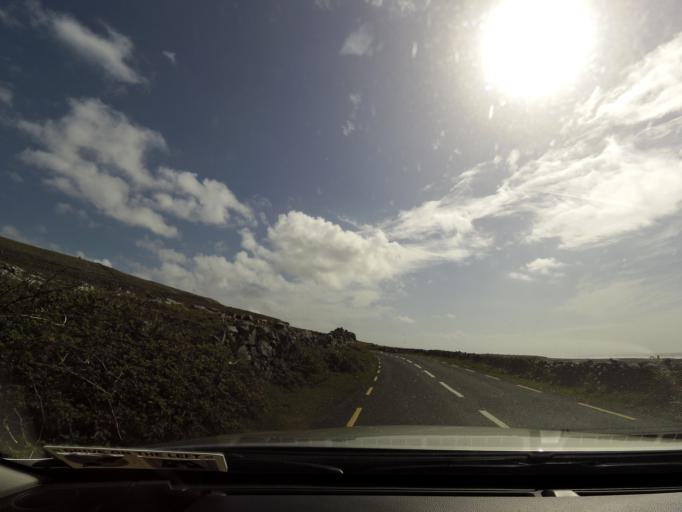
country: IE
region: Connaught
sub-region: County Galway
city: Bearna
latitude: 53.1480
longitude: -9.2708
